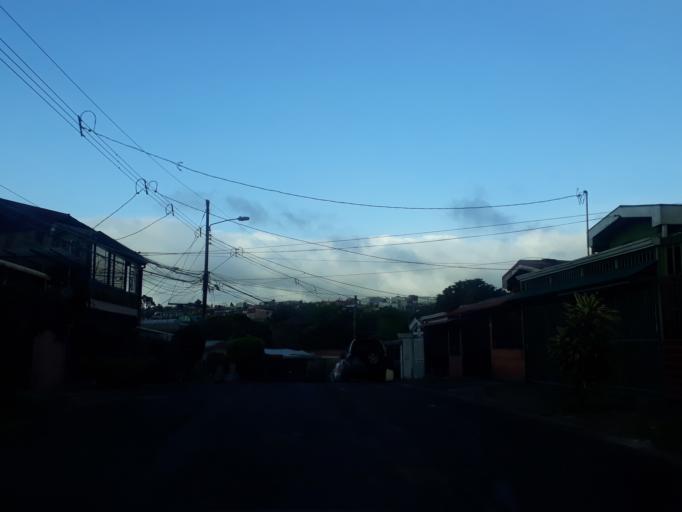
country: CR
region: San Jose
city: Purral
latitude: 9.9541
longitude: -84.0339
